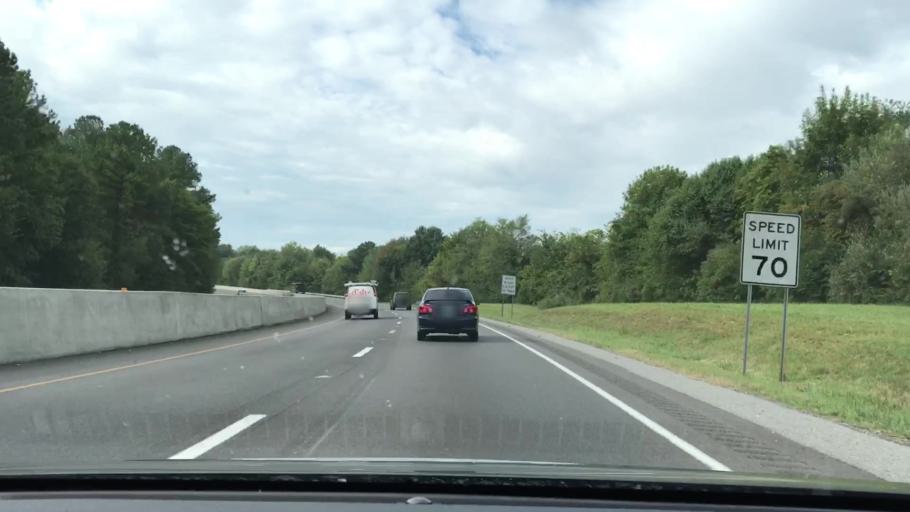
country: US
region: Kentucky
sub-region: Graves County
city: Mayfield
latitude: 36.7499
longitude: -88.6660
